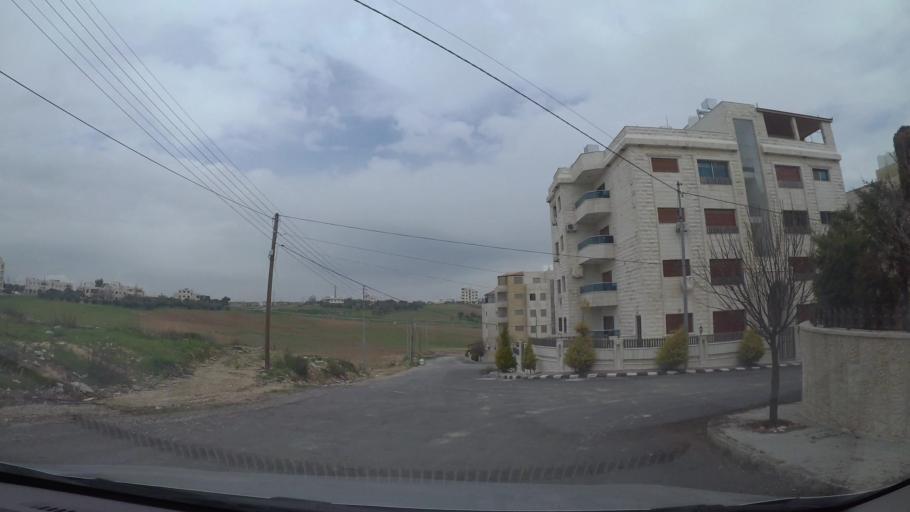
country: JO
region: Amman
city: Umm as Summaq
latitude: 31.9058
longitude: 35.8392
